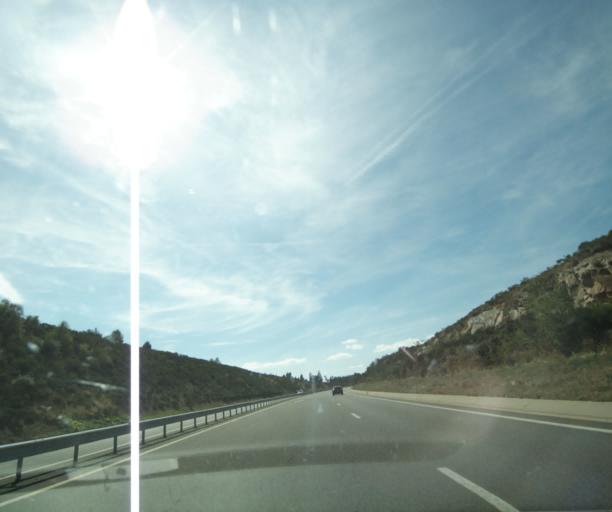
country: FR
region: Auvergne
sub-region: Departement du Puy-de-Dome
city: Gelles
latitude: 45.7947
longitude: 2.7634
